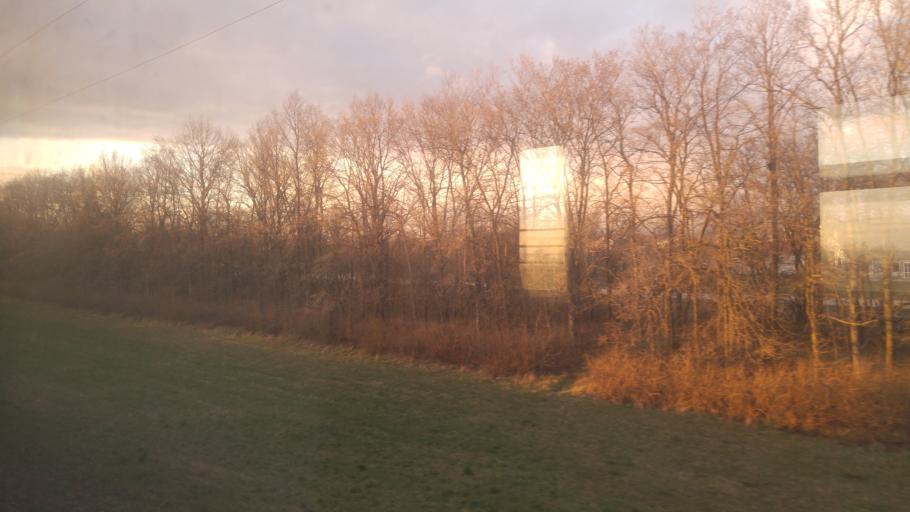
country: BY
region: Minsk
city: Rudzyensk
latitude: 53.6559
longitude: 27.7688
